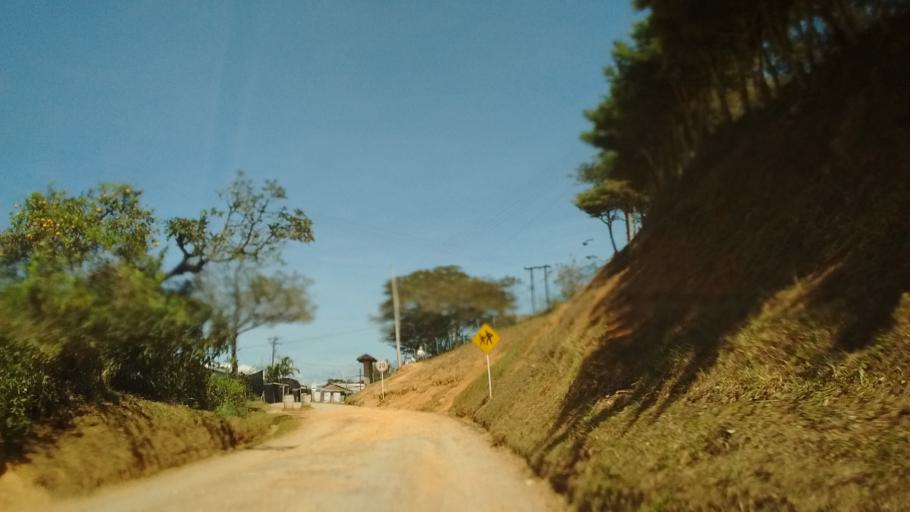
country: CO
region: Cauca
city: Lopez
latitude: 2.3960
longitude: -76.7467
